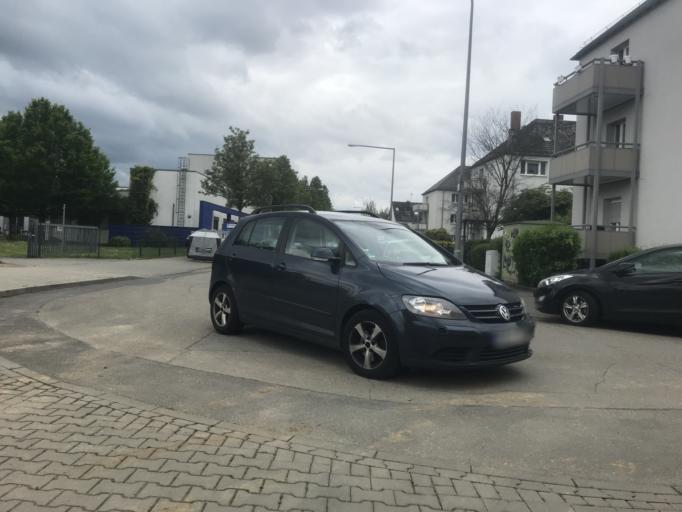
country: DE
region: Hesse
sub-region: Regierungsbezirk Darmstadt
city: Wiesbaden
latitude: 50.0395
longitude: 8.2466
